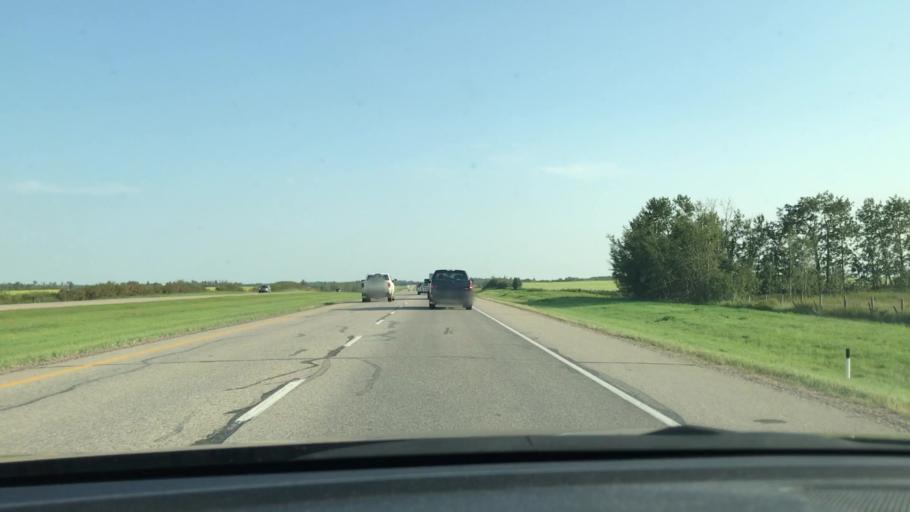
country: CA
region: Alberta
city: Millet
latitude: 53.0696
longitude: -113.5985
